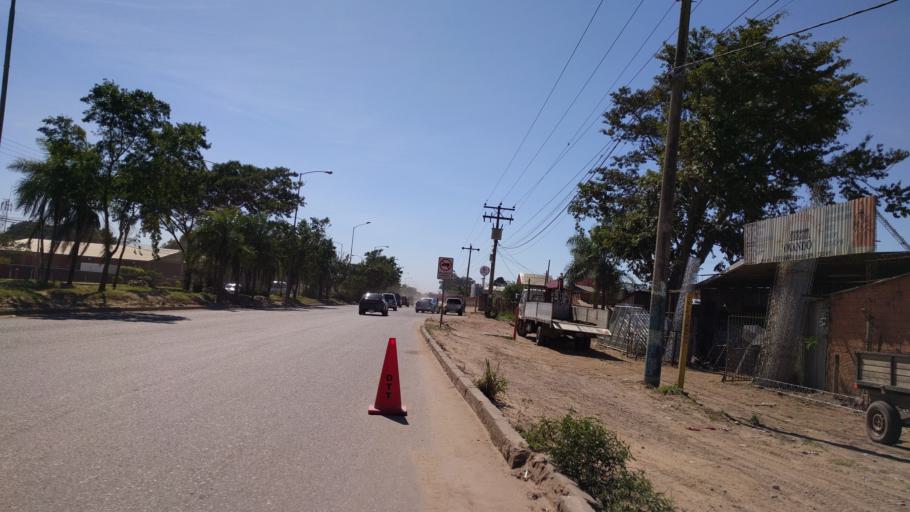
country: BO
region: Santa Cruz
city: Santa Cruz de la Sierra
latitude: -17.8353
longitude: -63.2346
